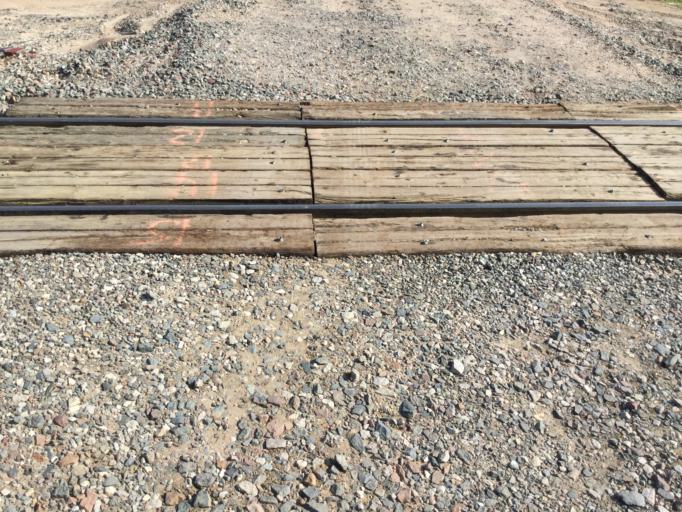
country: US
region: Kansas
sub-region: Pawnee County
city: Larned
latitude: 37.9576
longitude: -99.0406
